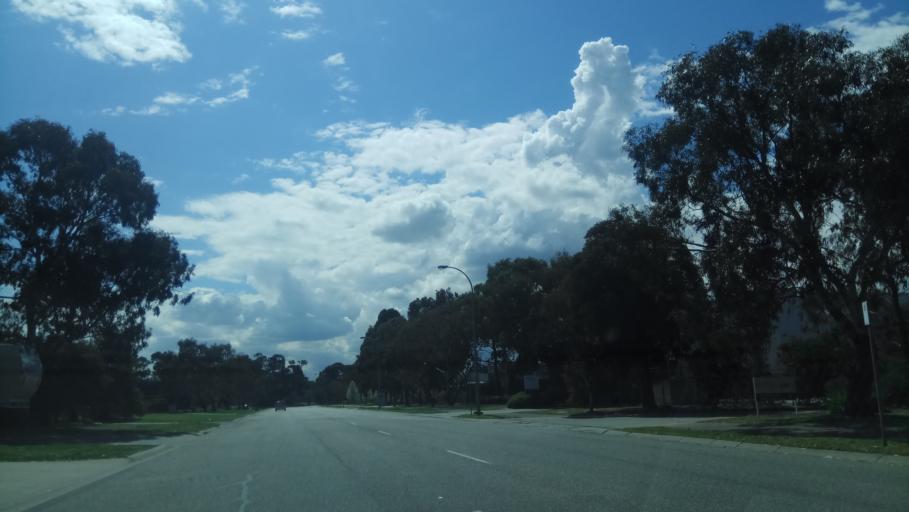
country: AU
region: Victoria
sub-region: Kingston
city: Dingley Village
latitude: -37.9931
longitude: 145.1184
